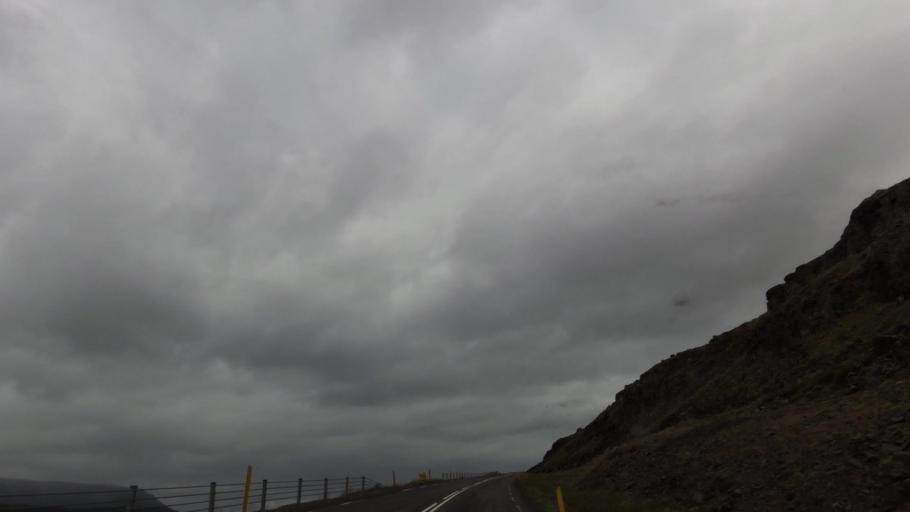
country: IS
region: Westfjords
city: Isafjoerdur
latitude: 65.9966
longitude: -22.7799
